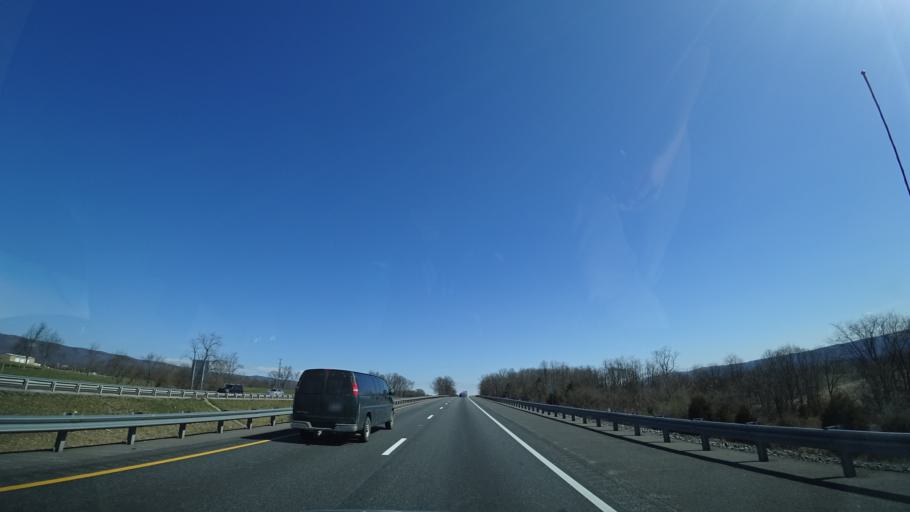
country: US
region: Virginia
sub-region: Shenandoah County
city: Woodstock
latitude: 38.8974
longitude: -78.5100
